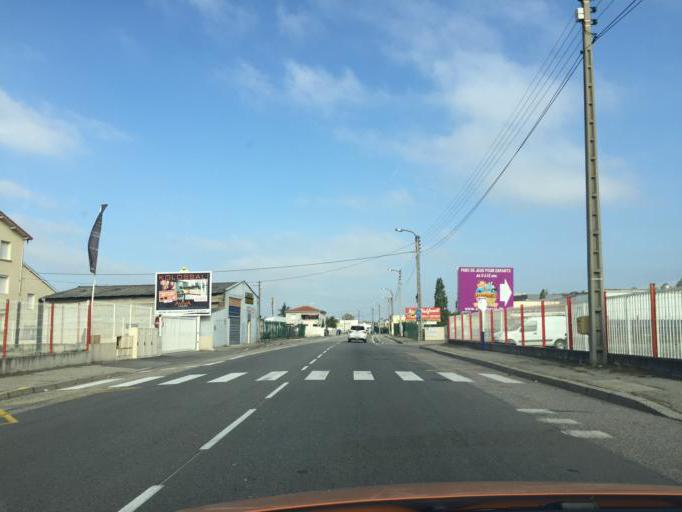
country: FR
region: Rhone-Alpes
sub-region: Departement de la Drome
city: Portes-les-Valence
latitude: 44.8982
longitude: 4.8839
